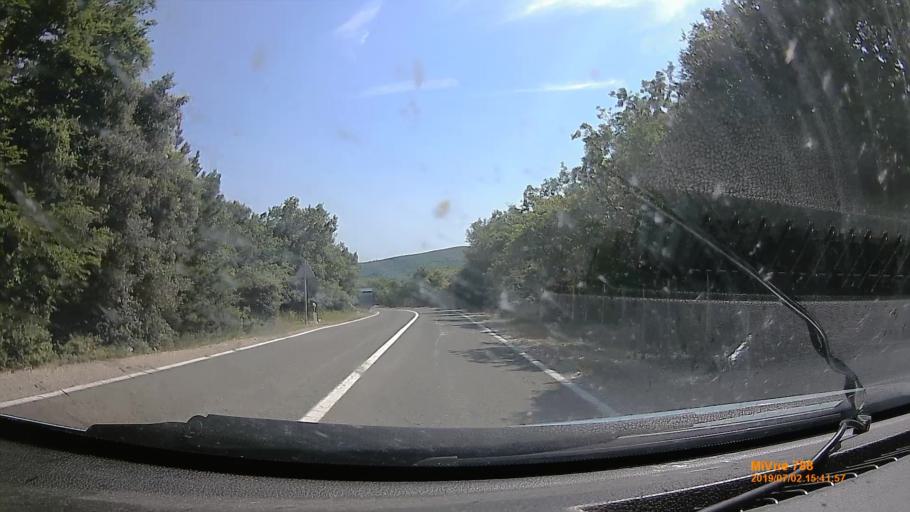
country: HR
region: Primorsko-Goranska
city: Cres
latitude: 44.9594
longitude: 14.4469
